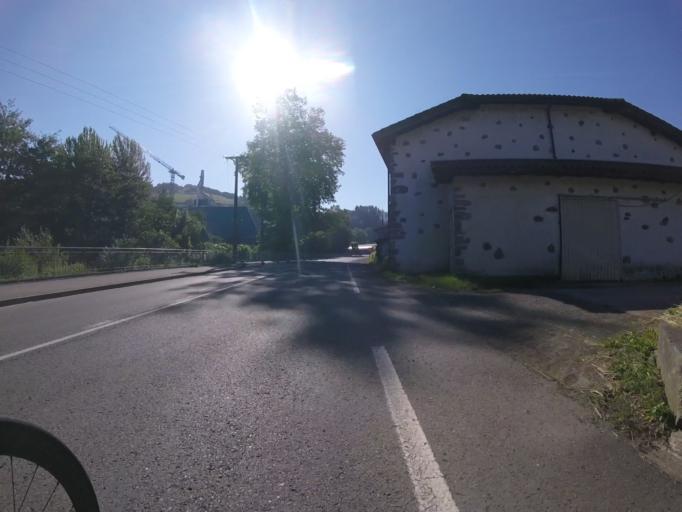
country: ES
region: Basque Country
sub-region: Provincia de Guipuzcoa
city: Azpeitia
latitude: 43.1703
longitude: -2.2541
